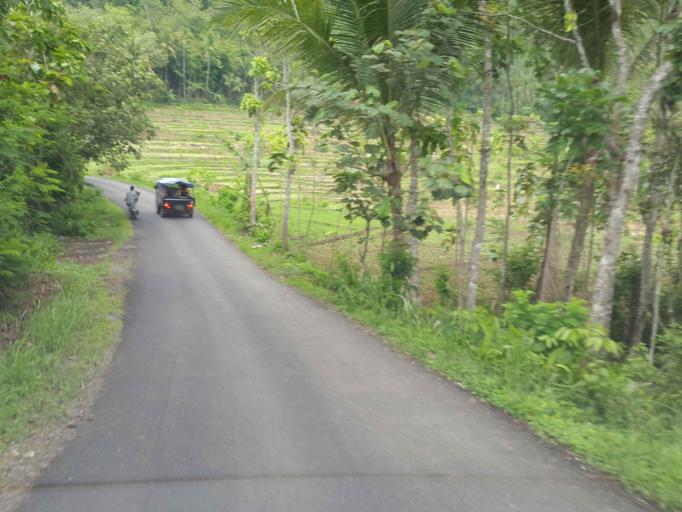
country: ID
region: Central Java
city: Genteng Wetan
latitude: -7.3606
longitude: 108.9023
